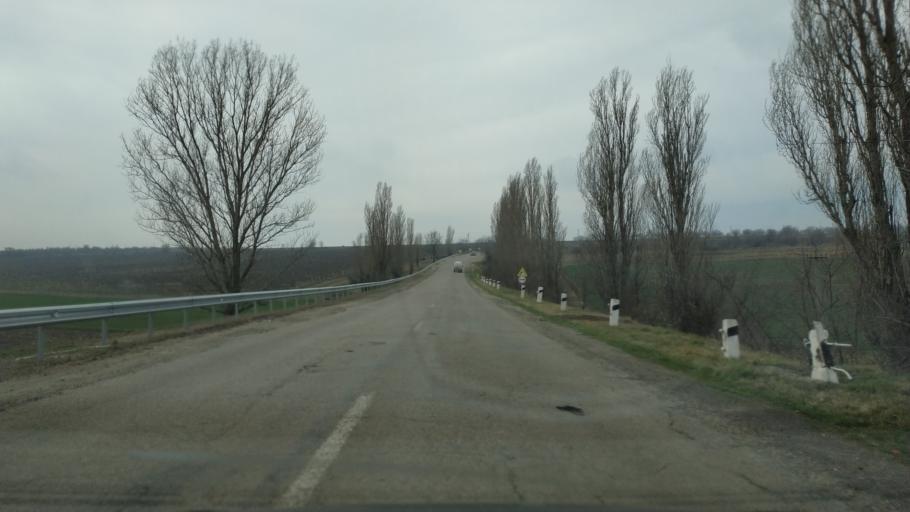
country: MD
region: Cahul
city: Cahul
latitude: 45.9555
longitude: 28.4027
